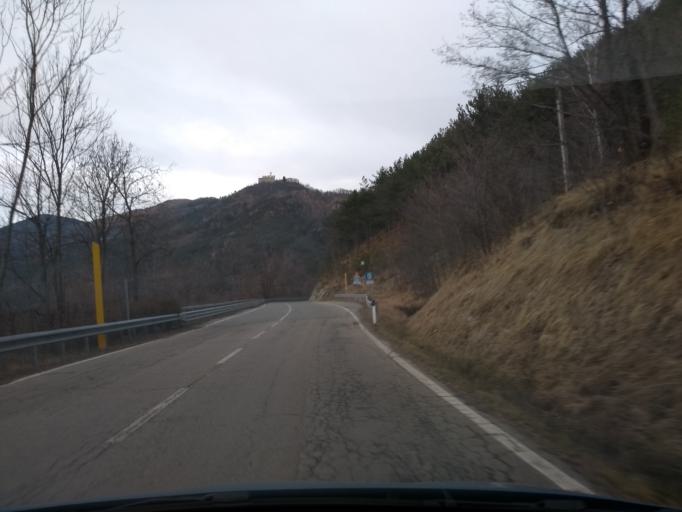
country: IT
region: Piedmont
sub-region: Provincia di Torino
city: La Villa
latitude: 45.2640
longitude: 7.4406
